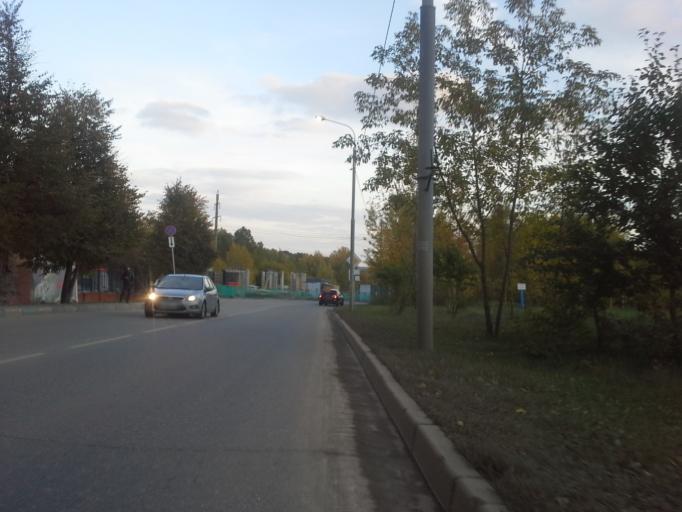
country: RU
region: Moskovskaya
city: Kommunarka
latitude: 55.5792
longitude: 37.4824
